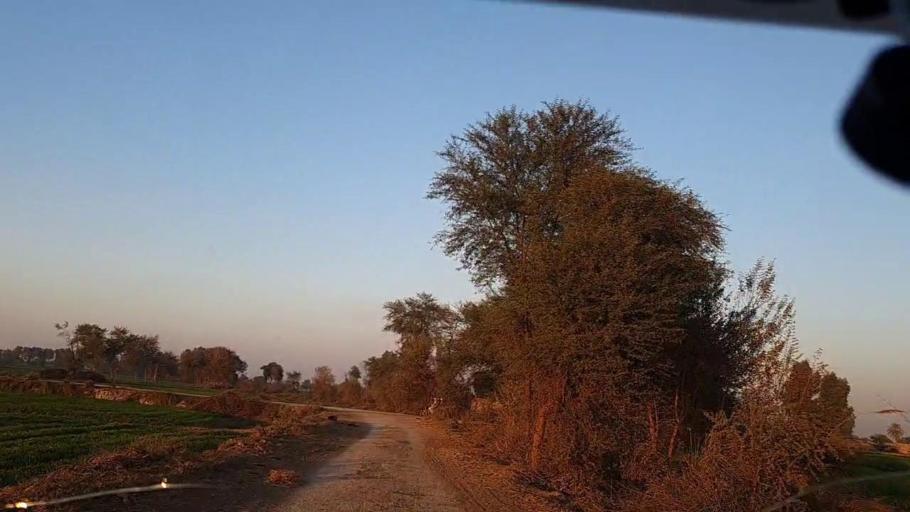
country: PK
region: Sindh
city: Adilpur
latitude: 27.8381
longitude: 69.2989
